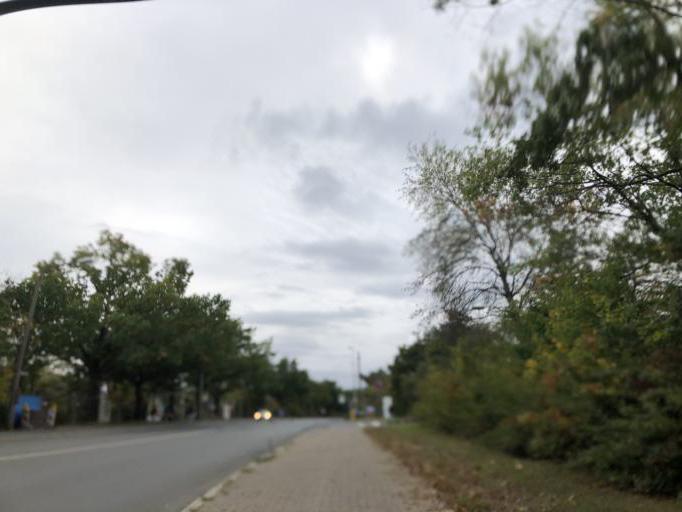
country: DE
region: Bavaria
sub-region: Regierungsbezirk Mittelfranken
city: Erlangen
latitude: 49.5801
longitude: 10.9671
